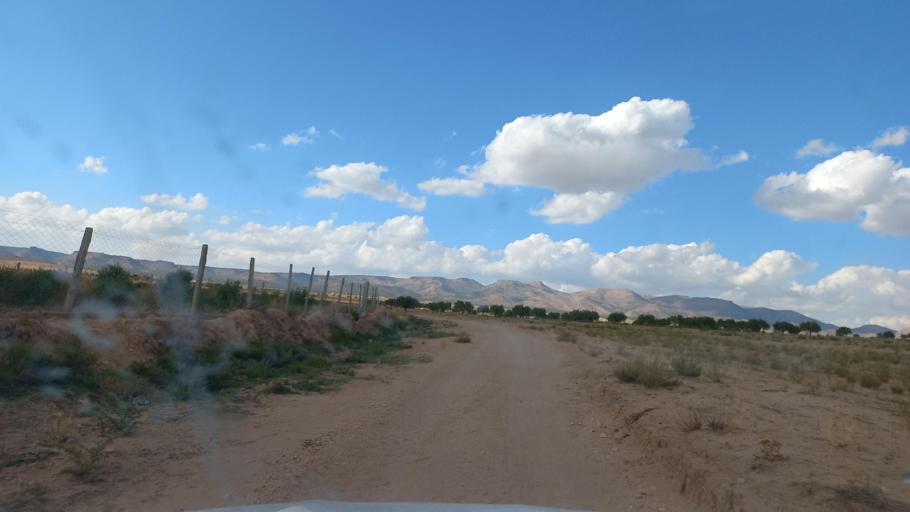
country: TN
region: Al Qasrayn
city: Sbiba
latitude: 35.3913
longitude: 9.0381
